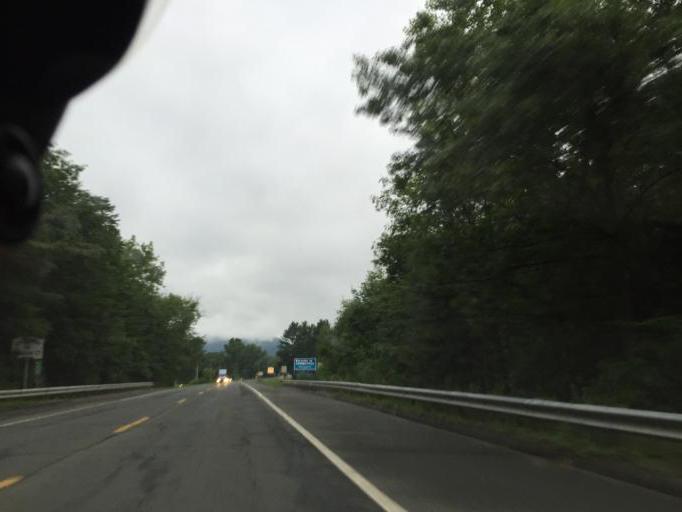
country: US
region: Connecticut
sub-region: Litchfield County
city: Canaan
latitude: 42.0484
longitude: -73.3257
